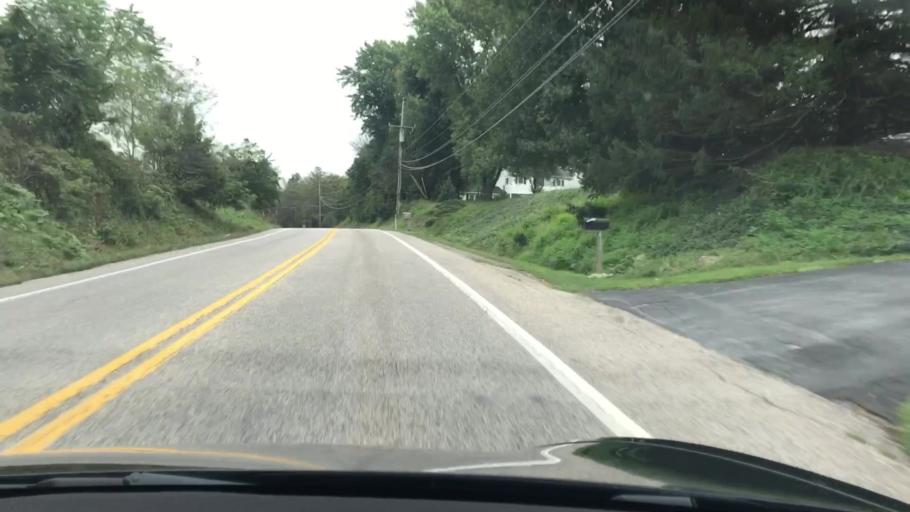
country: US
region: Pennsylvania
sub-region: Cumberland County
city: Mechanicsburg
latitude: 40.1626
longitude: -76.9757
